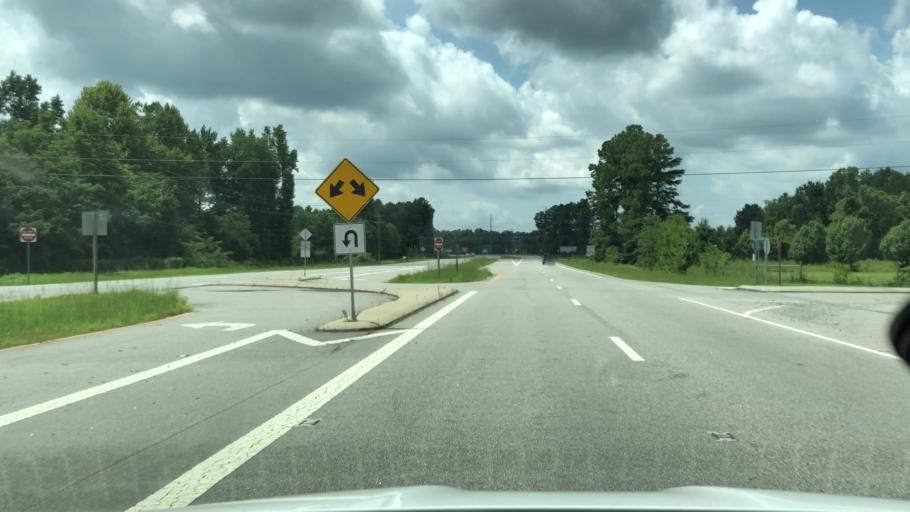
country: US
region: North Carolina
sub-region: Beaufort County
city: Washington
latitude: 35.4792
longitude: -77.1154
